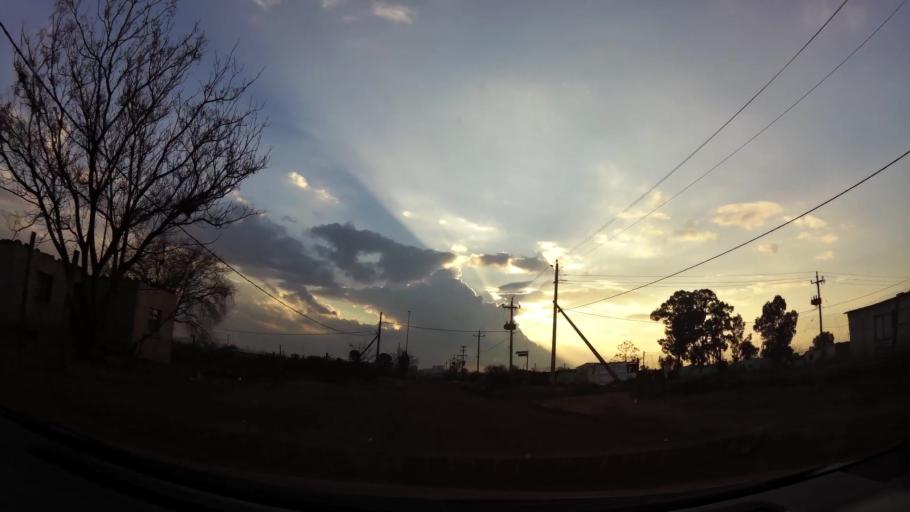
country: ZA
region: Gauteng
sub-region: City of Johannesburg Metropolitan Municipality
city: Orange Farm
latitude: -26.5402
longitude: 27.8479
